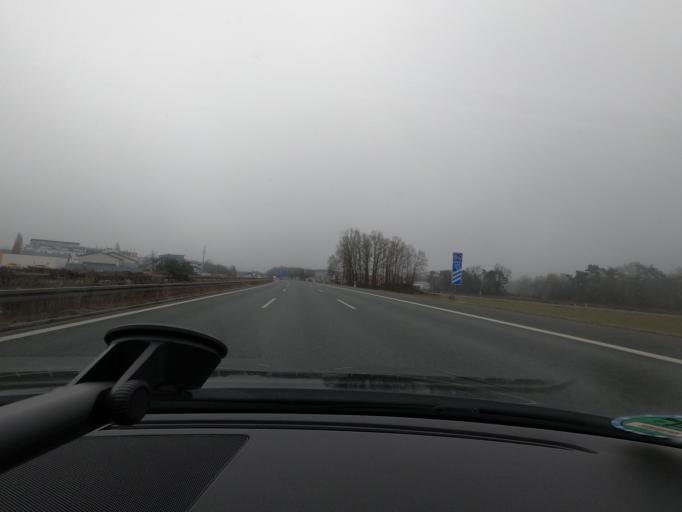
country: DE
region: Bavaria
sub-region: Regierungsbezirk Mittelfranken
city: Erlangen
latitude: 49.5423
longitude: 11.0203
